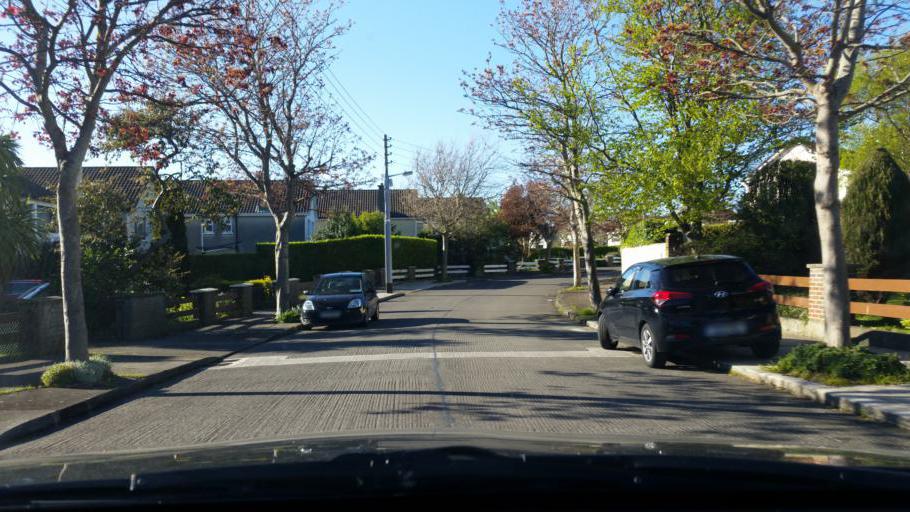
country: IE
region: Leinster
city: Sutton
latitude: 53.3752
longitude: -6.0965
